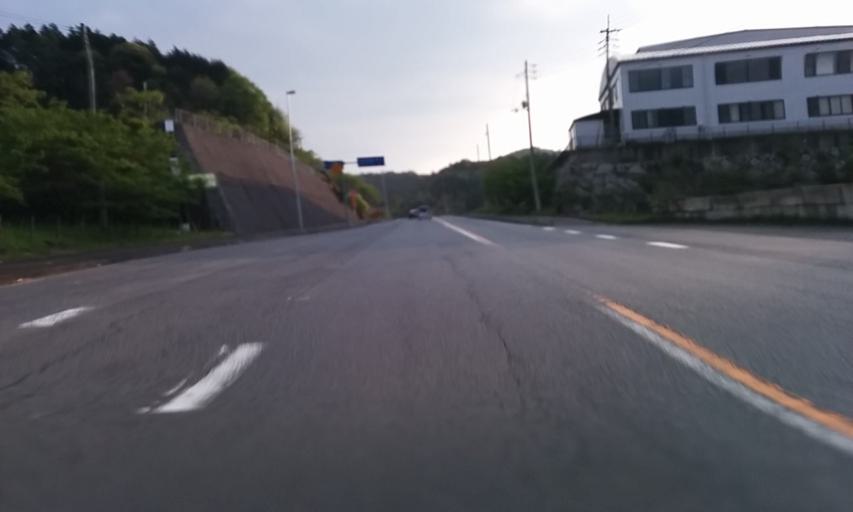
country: JP
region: Ehime
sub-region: Shikoku-chuo Shi
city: Matsuyama
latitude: 33.8067
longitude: 132.9724
